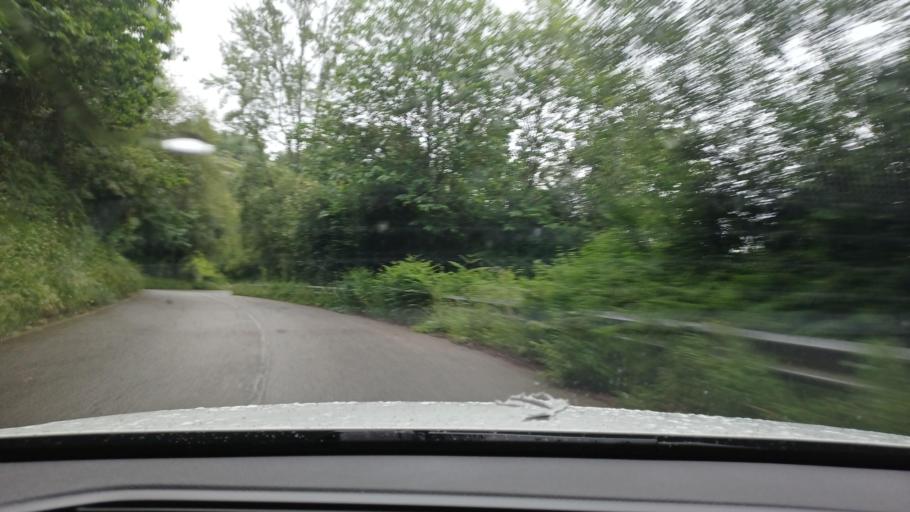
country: ES
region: Asturias
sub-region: Province of Asturias
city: Castandiello
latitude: 43.3138
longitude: -5.9260
